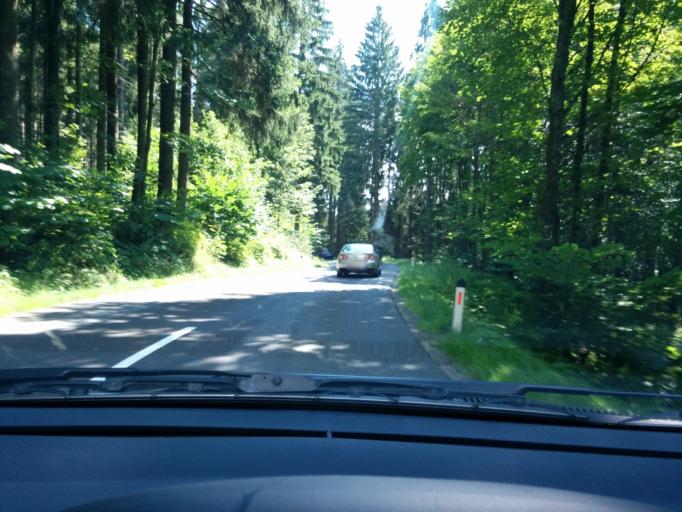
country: AT
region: Upper Austria
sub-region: Politischer Bezirk Rohrbach
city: Ulrichsberg
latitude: 48.7211
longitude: 13.8958
